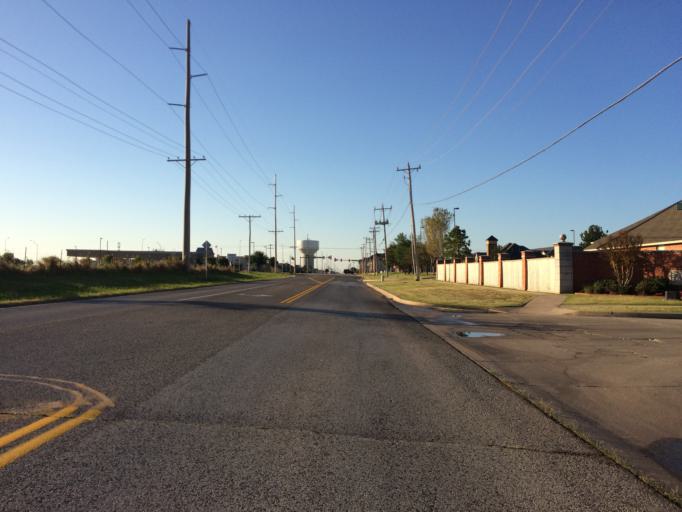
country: US
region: Oklahoma
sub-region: Cleveland County
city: Norman
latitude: 35.2642
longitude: -97.4944
